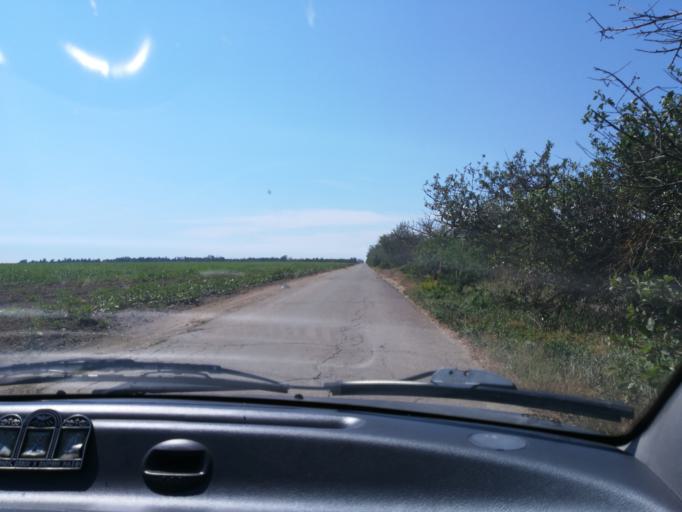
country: RU
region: Krasnodarskiy
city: Blagovetschenskaya
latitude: 45.0590
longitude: 37.0988
